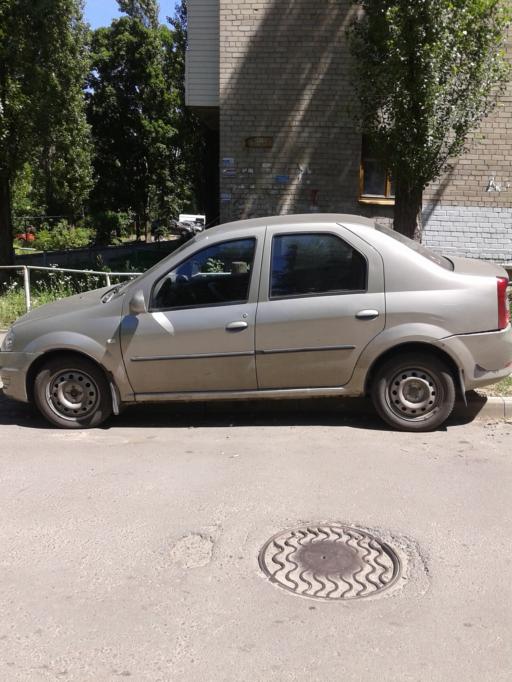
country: RU
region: Voronezj
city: Voronezh
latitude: 51.6523
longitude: 39.1414
